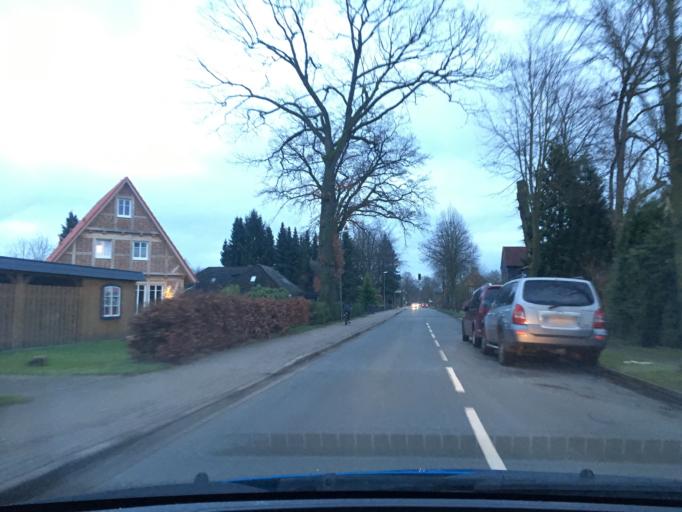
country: DE
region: Lower Saxony
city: Radbruch
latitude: 53.3105
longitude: 10.2857
